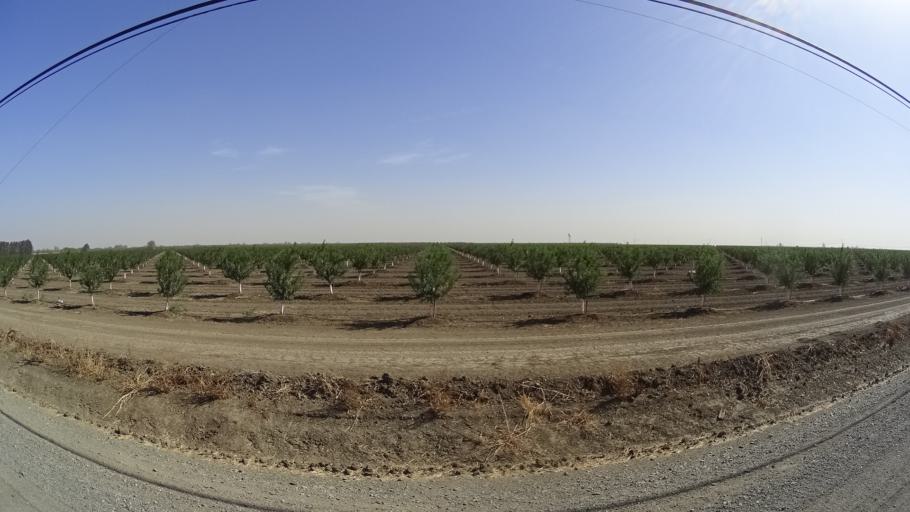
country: US
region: California
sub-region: Yolo County
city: Davis
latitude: 38.5054
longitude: -121.6954
